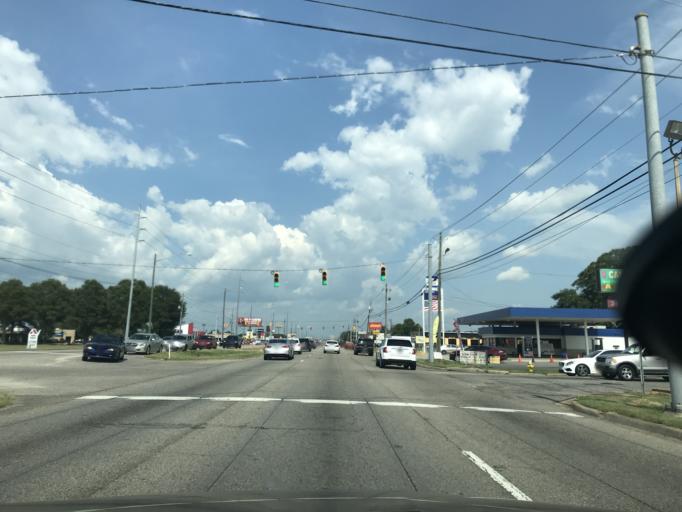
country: US
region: Alabama
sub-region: Montgomery County
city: Montgomery
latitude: 32.3819
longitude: -86.2057
